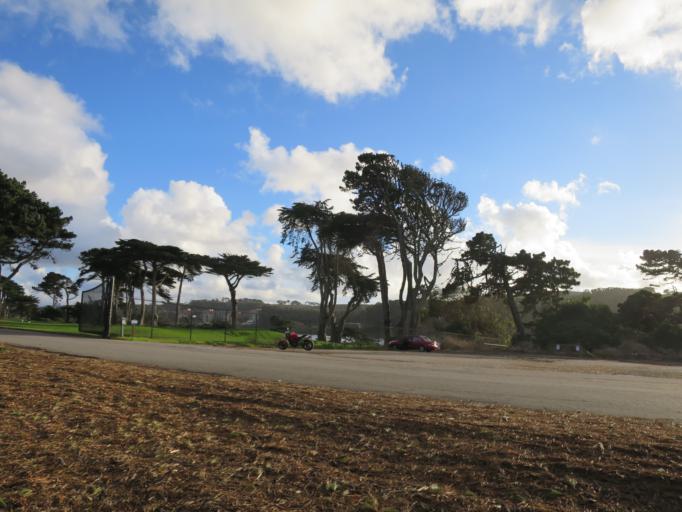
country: US
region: California
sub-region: San Mateo County
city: Daly City
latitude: 37.7254
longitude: -122.4984
